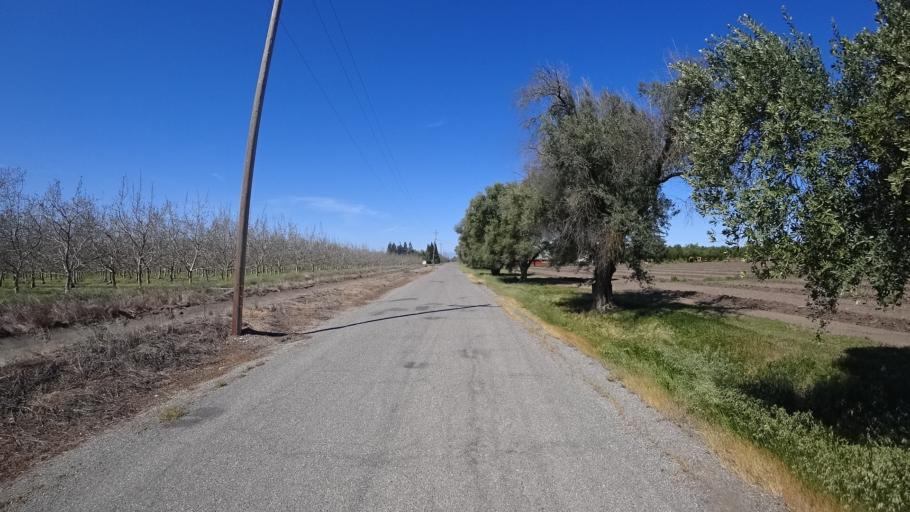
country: US
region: California
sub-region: Glenn County
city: Orland
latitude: 39.7431
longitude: -122.1161
